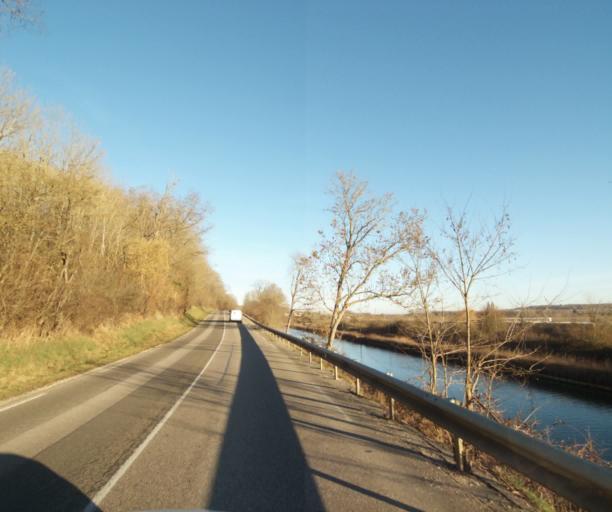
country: FR
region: Lorraine
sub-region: Departement de Meurthe-et-Moselle
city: Art-sur-Meurthe
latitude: 48.6459
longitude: 6.2845
